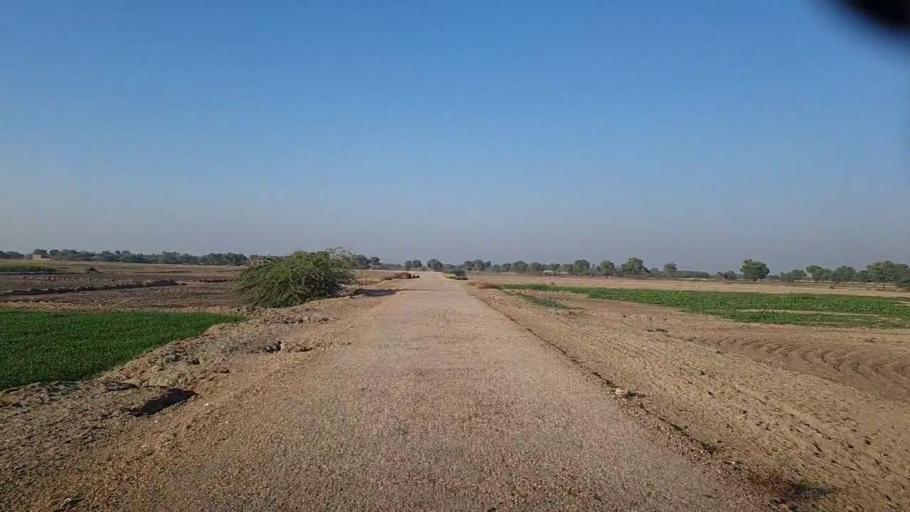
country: PK
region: Sindh
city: Pad Idan
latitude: 26.7316
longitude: 68.3492
